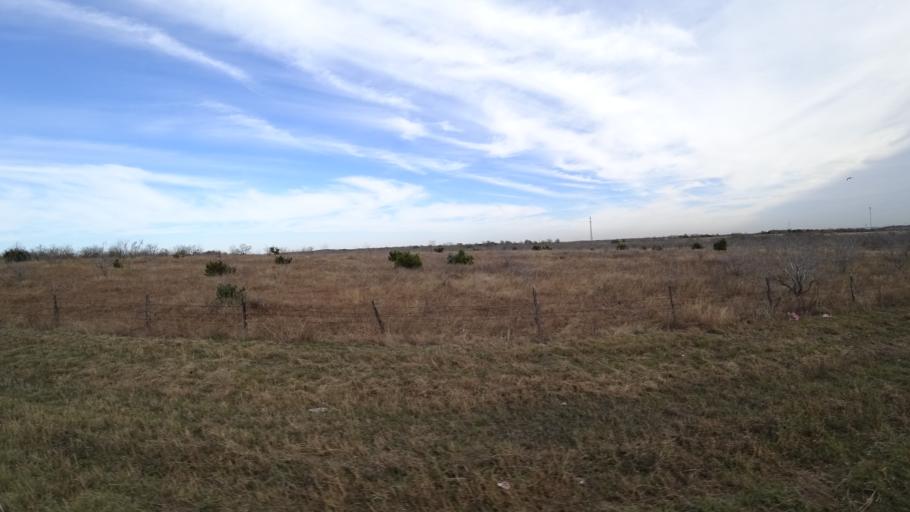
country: US
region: Texas
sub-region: Travis County
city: Onion Creek
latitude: 30.1309
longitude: -97.7140
